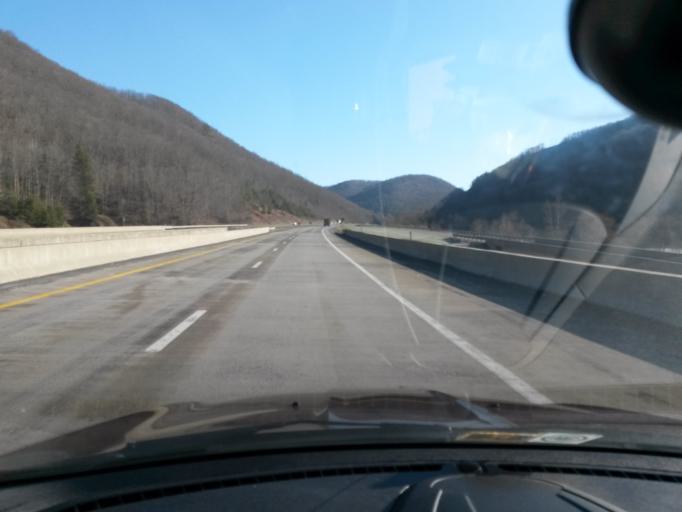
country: US
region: West Virginia
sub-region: Braxton County
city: Sutton
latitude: 38.5003
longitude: -80.7555
